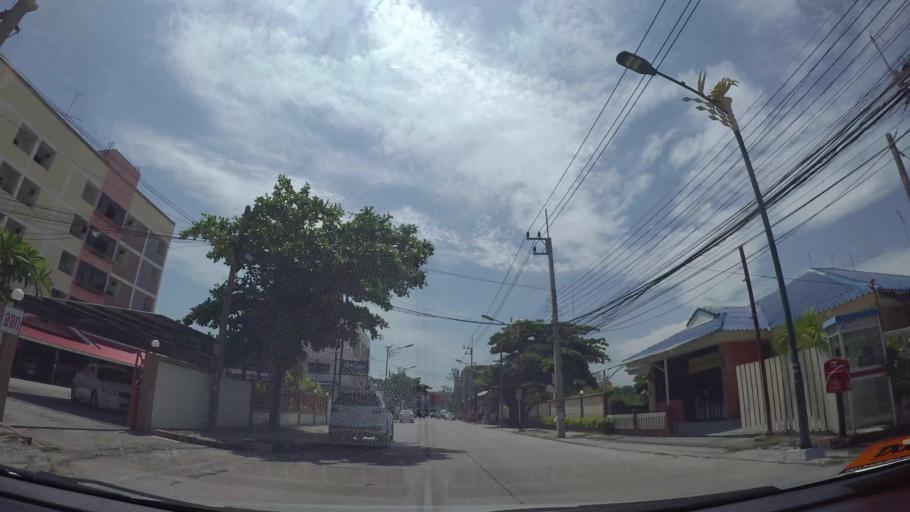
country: TH
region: Chon Buri
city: Chon Buri
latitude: 13.3307
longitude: 100.9502
